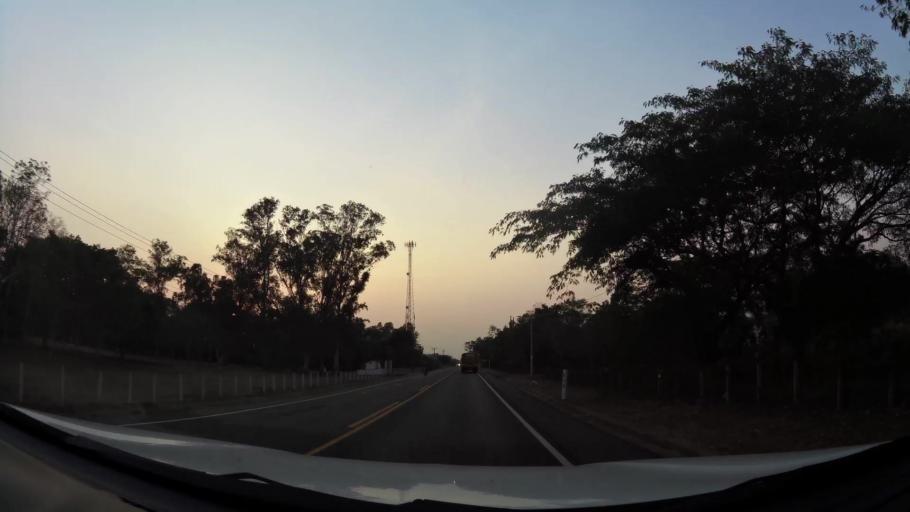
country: NI
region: Leon
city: Leon
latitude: 12.3359
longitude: -86.8115
